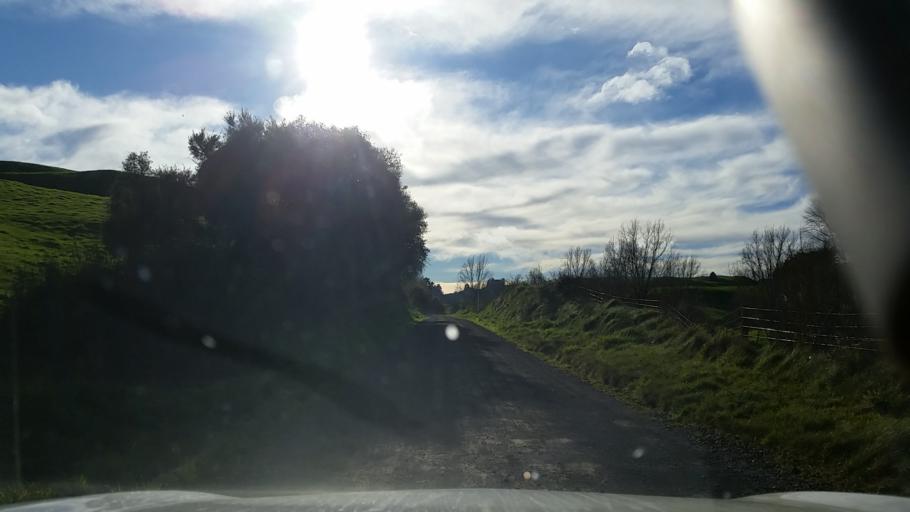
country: NZ
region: Waikato
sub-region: South Waikato District
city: Tokoroa
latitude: -38.3926
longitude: 176.0747
